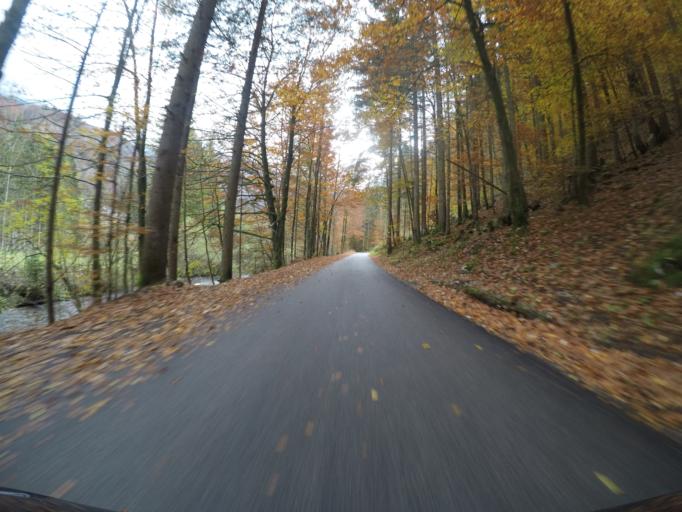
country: SI
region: Jesenice
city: Hrusica
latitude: 46.4181
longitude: 13.9849
